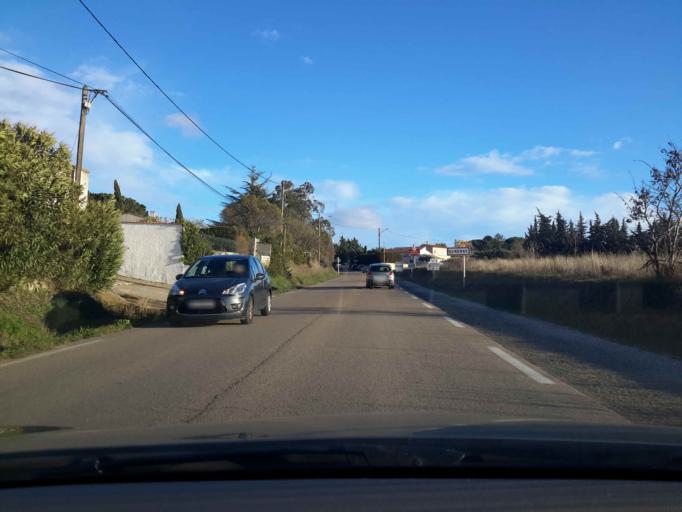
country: FR
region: Languedoc-Roussillon
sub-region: Departement du Gard
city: Generac
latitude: 43.7371
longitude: 4.3444
